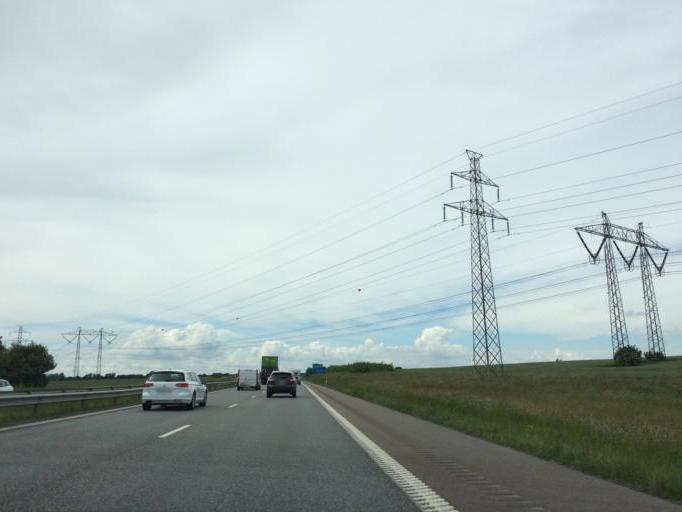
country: SE
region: Skane
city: Bjarred
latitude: 55.7414
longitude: 13.0444
